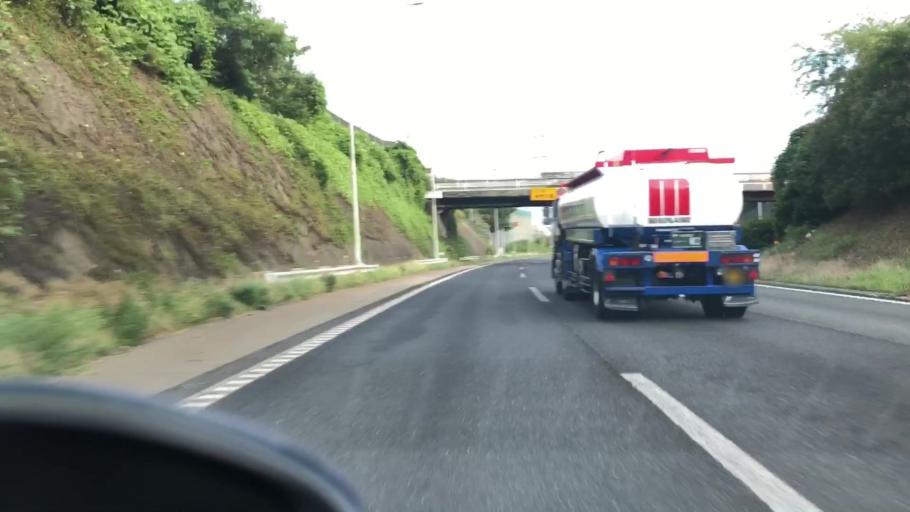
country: JP
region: Hyogo
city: Takarazuka
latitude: 34.8168
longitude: 135.3546
